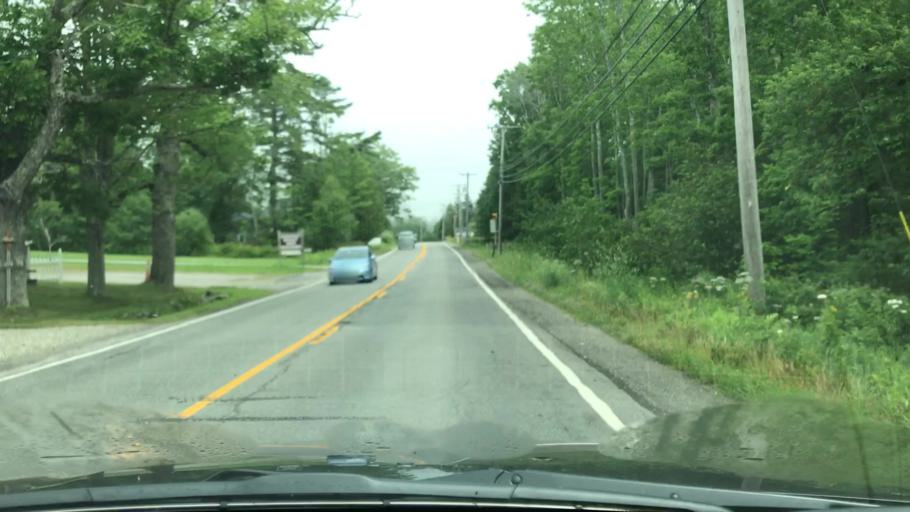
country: US
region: Maine
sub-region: Waldo County
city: Lincolnville
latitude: 44.2985
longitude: -69.0014
